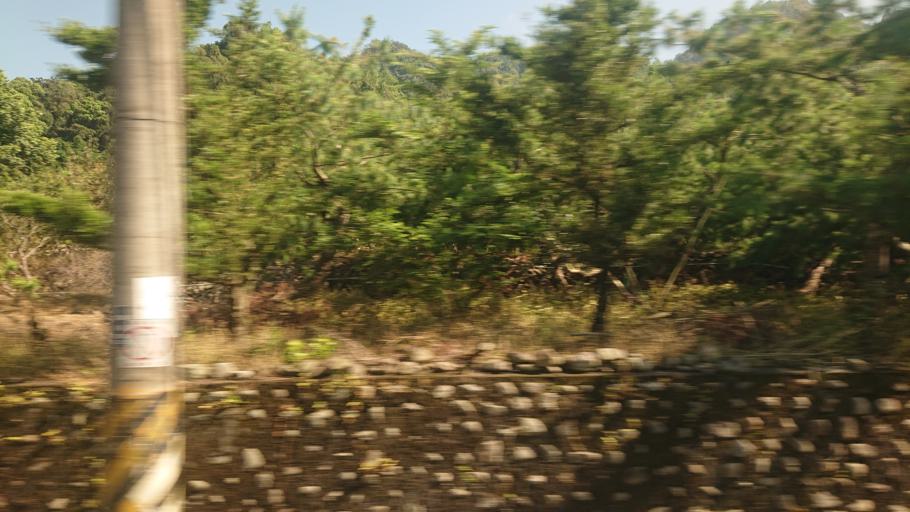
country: TW
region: Taiwan
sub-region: Nantou
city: Puli
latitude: 24.0612
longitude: 120.8936
